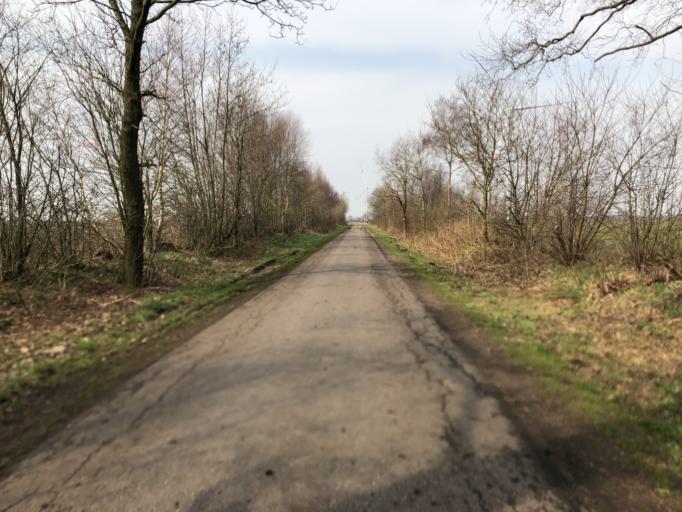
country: DE
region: Schleswig-Holstein
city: Wanderup
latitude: 54.6828
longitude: 9.3077
